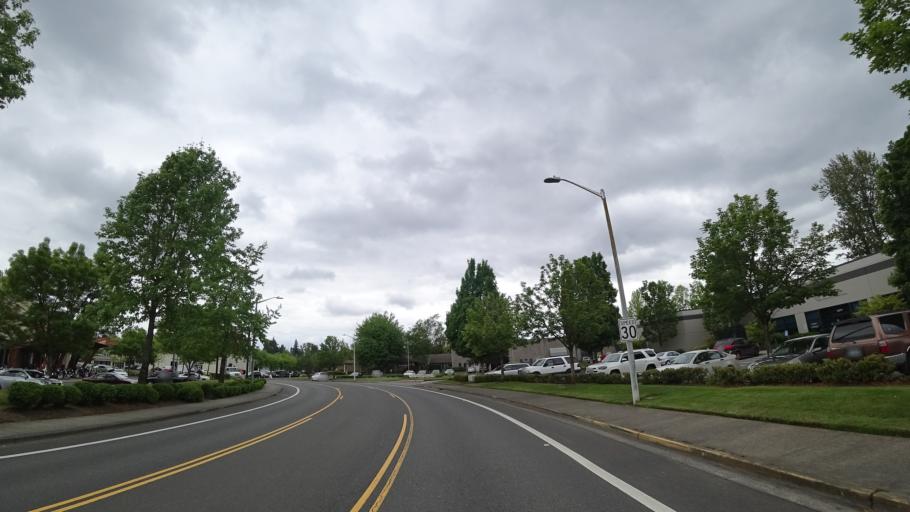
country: US
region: Oregon
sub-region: Washington County
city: Tigard
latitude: 45.4427
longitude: -122.7820
